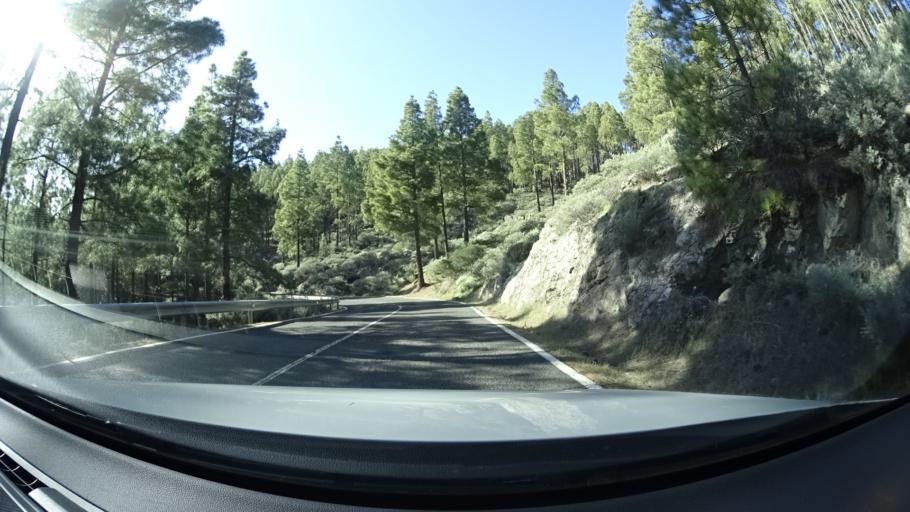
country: ES
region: Canary Islands
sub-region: Provincia de Las Palmas
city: Vega de San Mateo
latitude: 27.9667
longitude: -15.5447
